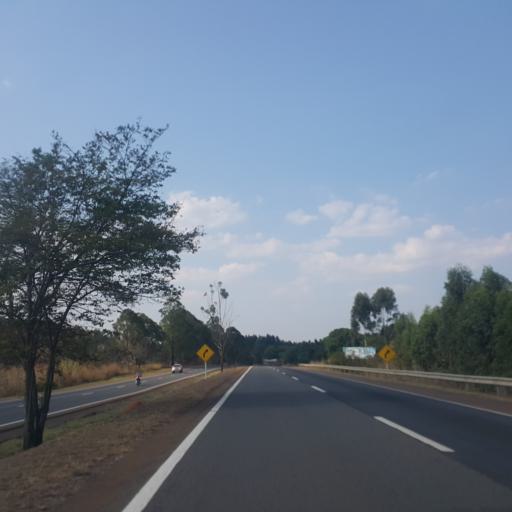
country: BR
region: Goias
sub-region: Abadiania
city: Abadiania
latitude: -16.1869
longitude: -48.6988
